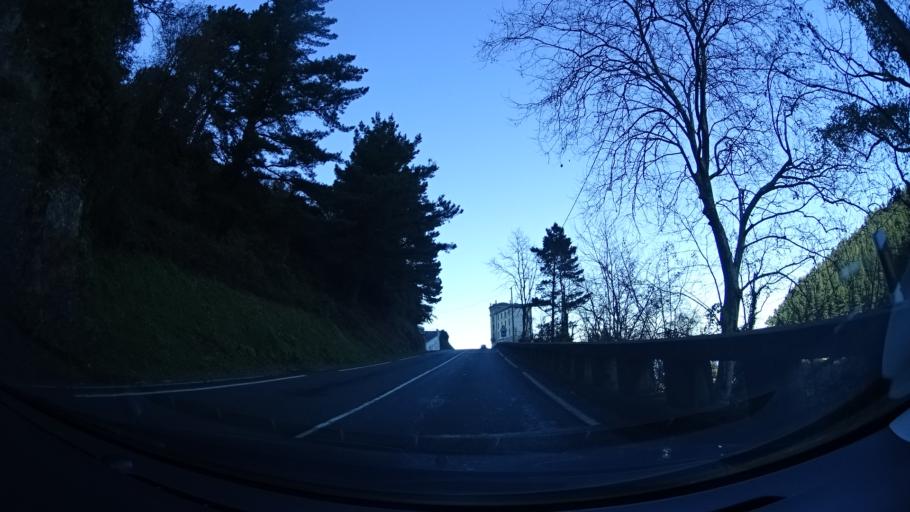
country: ES
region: Basque Country
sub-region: Bizkaia
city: Ondarroa
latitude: 43.3192
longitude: -2.4131
